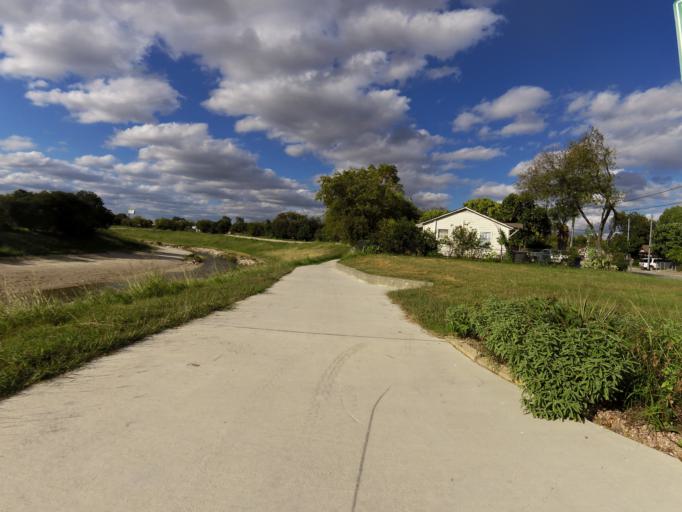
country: US
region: Texas
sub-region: Bexar County
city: San Antonio
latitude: 29.4015
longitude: -98.5062
